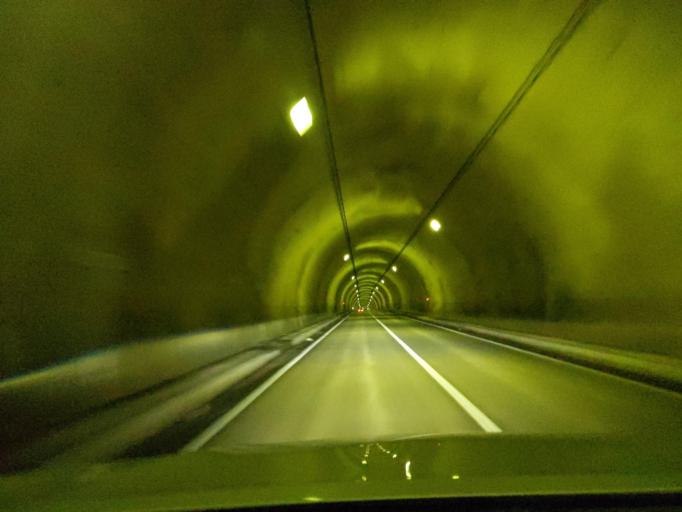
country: JP
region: Niigata
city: Nagaoka
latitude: 37.4454
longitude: 138.6933
